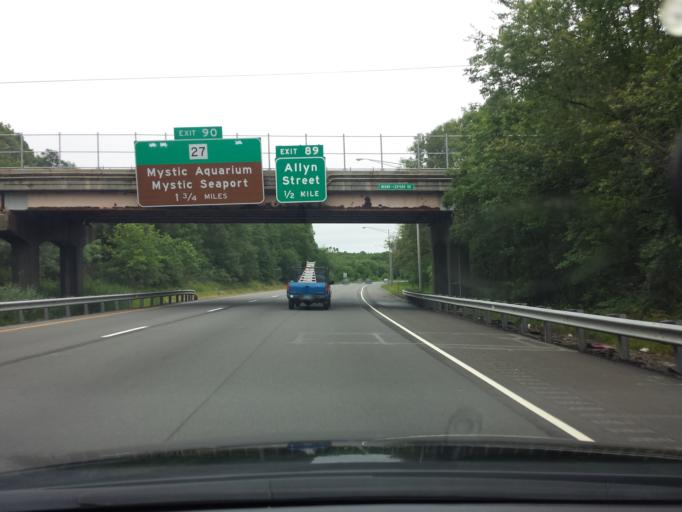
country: US
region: Connecticut
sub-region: New London County
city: Mystic
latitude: 41.3711
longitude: -71.9968
